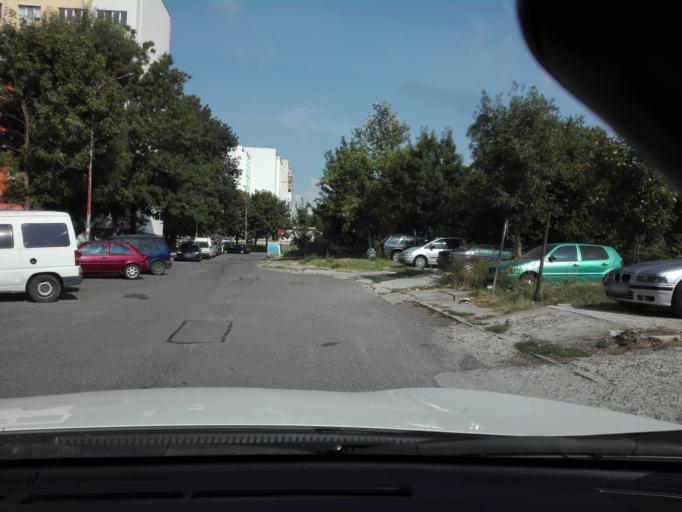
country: BG
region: Burgas
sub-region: Obshtina Burgas
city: Burgas
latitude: 42.4536
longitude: 27.4238
